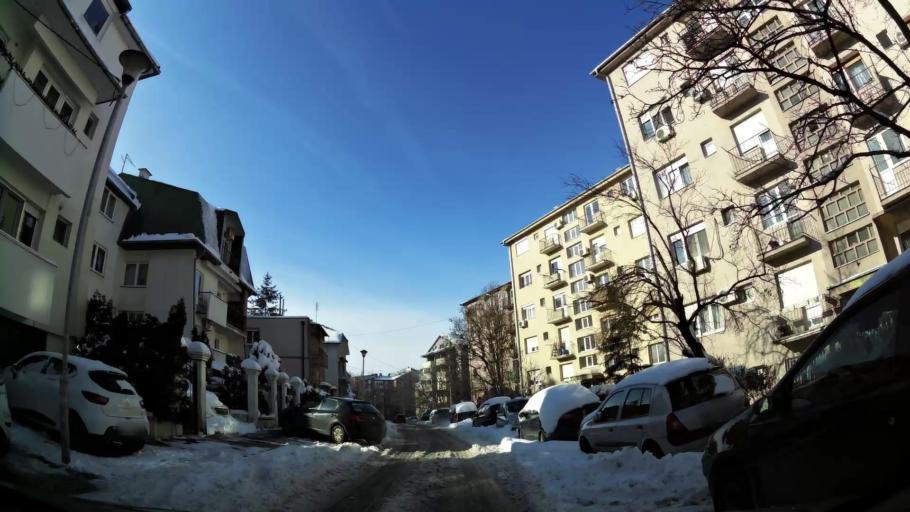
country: RS
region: Central Serbia
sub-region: Belgrade
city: Palilula
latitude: 44.8120
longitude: 20.5122
